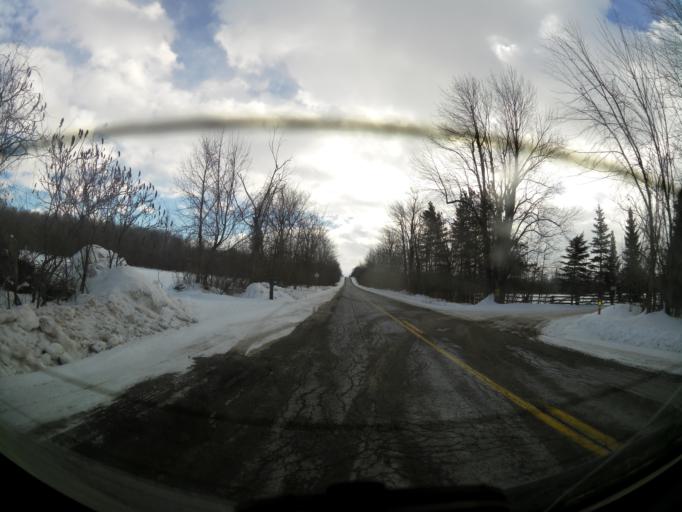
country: CA
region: Ontario
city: Ottawa
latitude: 45.2600
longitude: -75.4586
